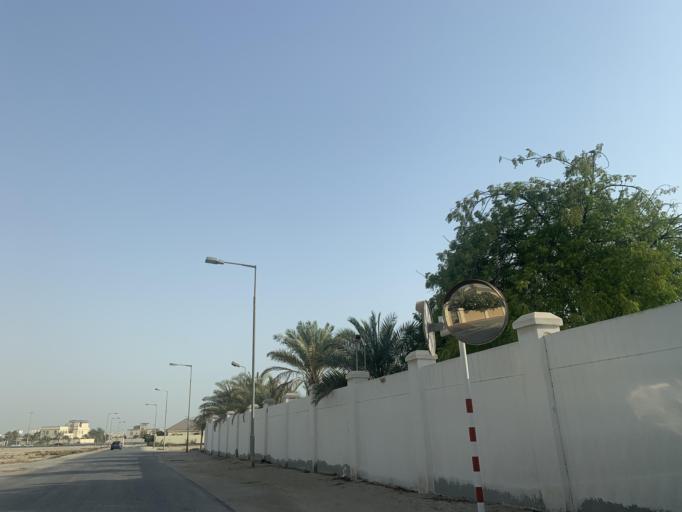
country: BH
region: Central Governorate
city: Madinat Hamad
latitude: 26.1760
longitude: 50.4740
